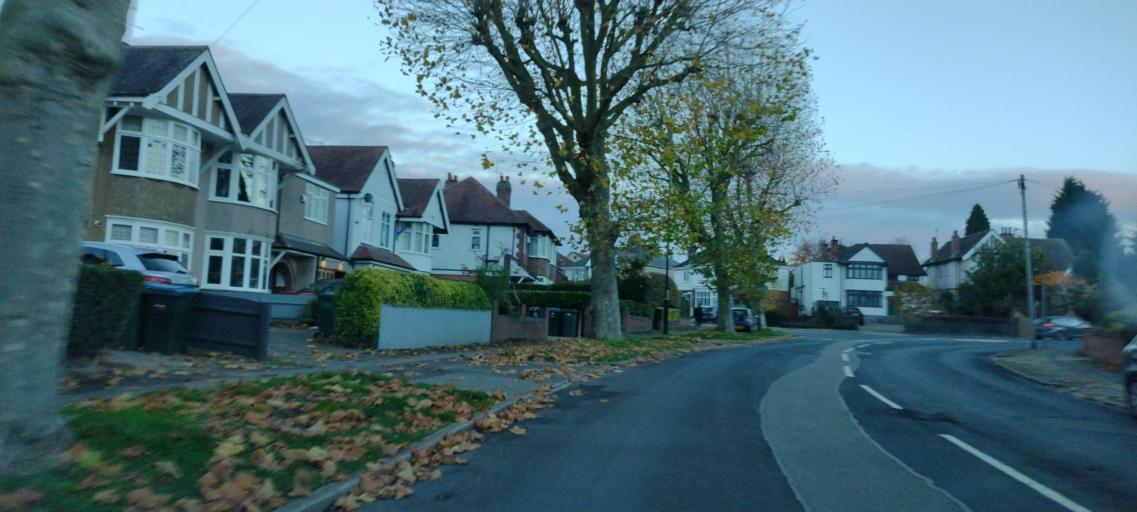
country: GB
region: England
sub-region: Coventry
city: Coventry
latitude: 52.3998
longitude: -1.5385
